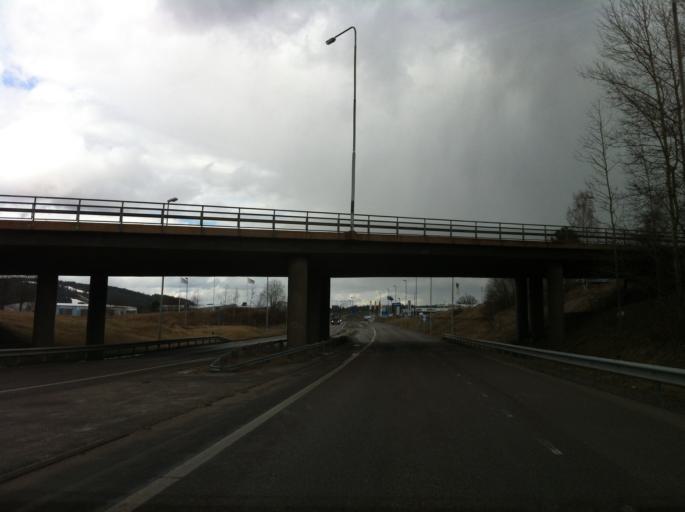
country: SE
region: Vaestra Goetaland
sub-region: Ulricehamns Kommun
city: Ulricehamn
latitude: 57.7376
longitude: 13.4337
